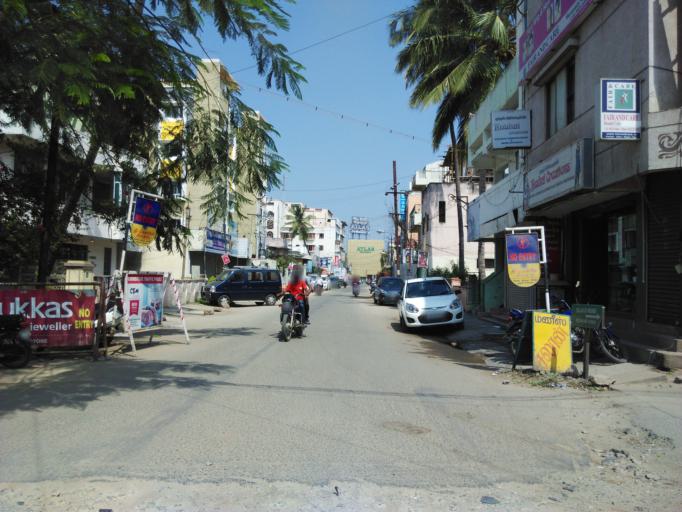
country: IN
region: Tamil Nadu
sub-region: Coimbatore
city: Coimbatore
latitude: 11.0153
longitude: 76.9633
